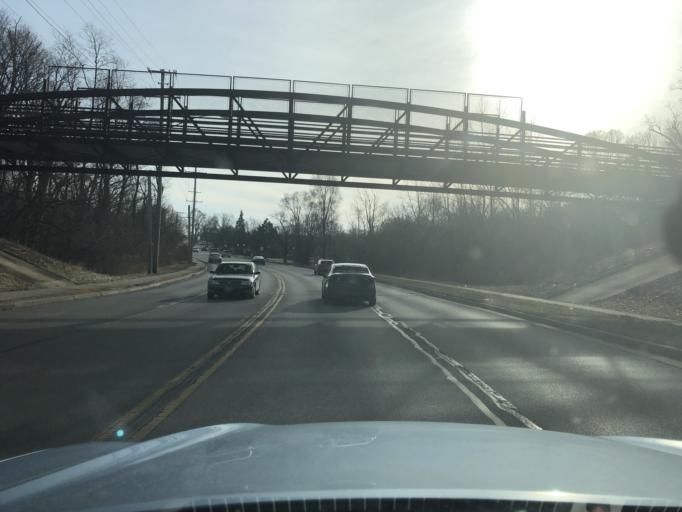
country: US
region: Illinois
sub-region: DuPage County
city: Bloomingdale
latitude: 41.9631
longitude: -88.0823
